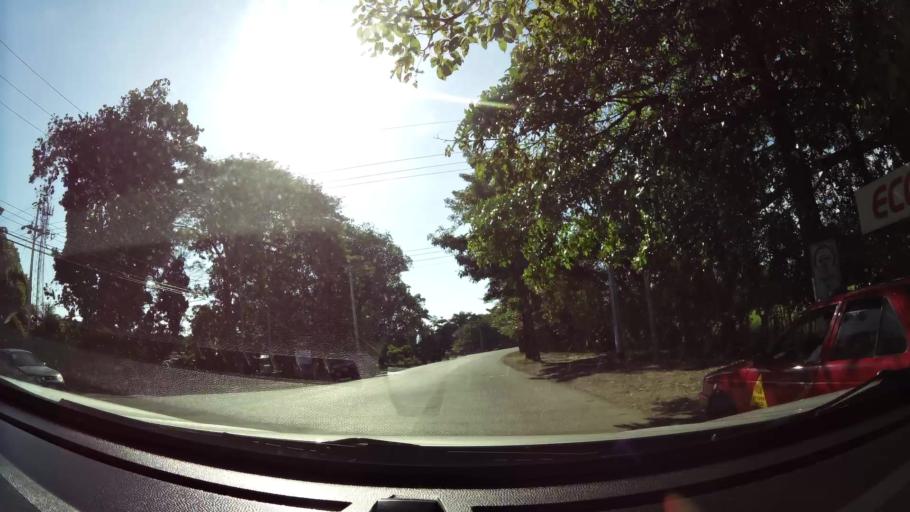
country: CR
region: Puntarenas
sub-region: Canton de Garabito
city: Jaco
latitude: 9.6103
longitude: -84.6224
